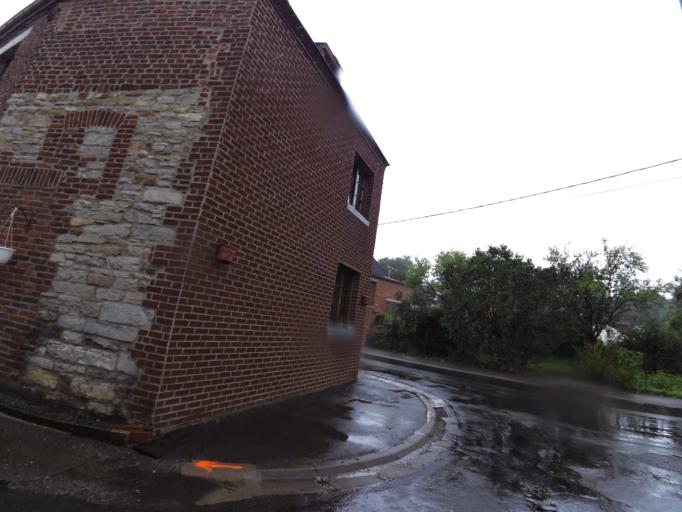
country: BE
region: Wallonia
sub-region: Province de Namur
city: Rochefort
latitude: 50.1617
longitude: 5.2259
